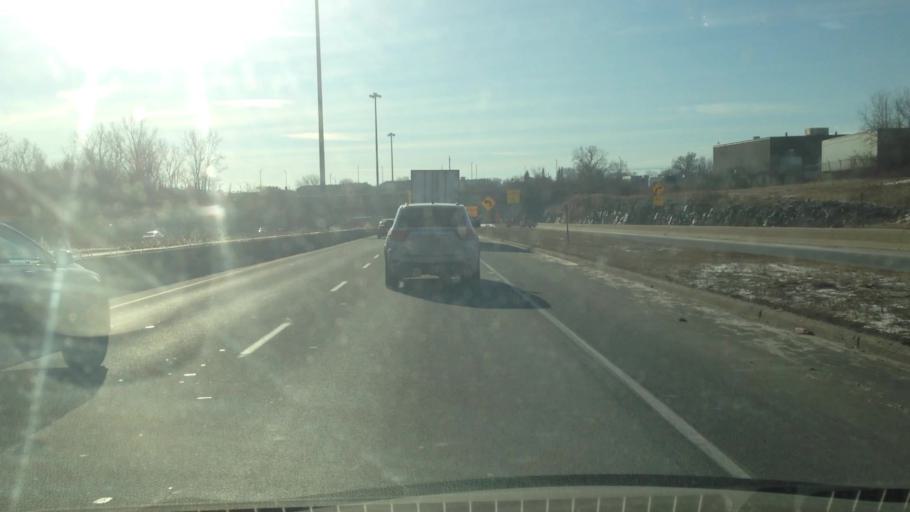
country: CA
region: Quebec
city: Cote-Saint-Luc
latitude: 45.4518
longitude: -73.6974
